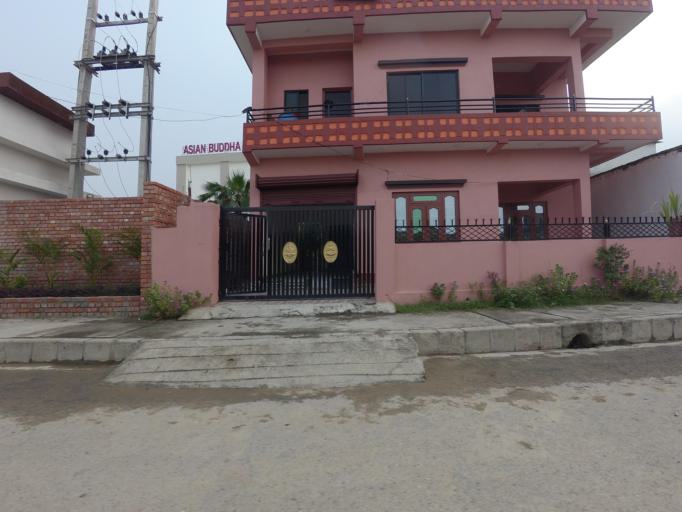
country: NP
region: Western Region
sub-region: Lumbini Zone
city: Bhairahawa
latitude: 27.5185
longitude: 83.4429
